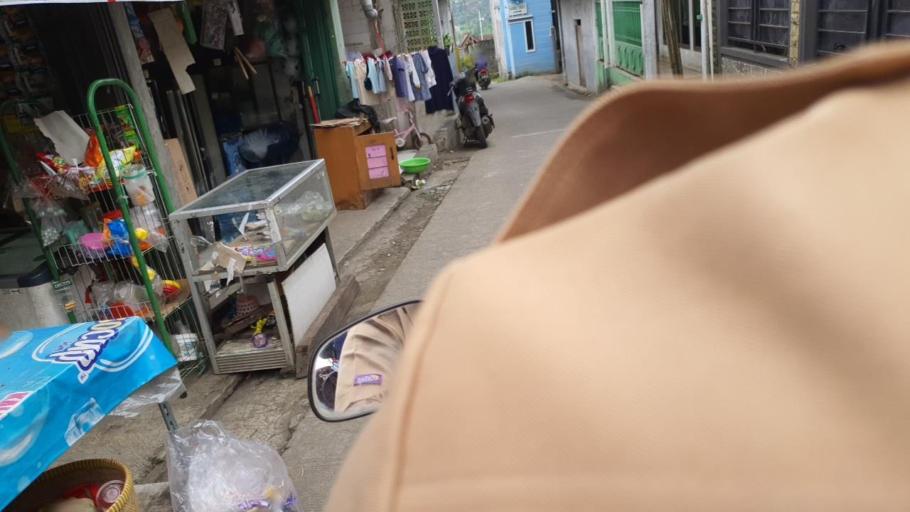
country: ID
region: West Java
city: Caringin
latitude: -6.6508
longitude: 106.8868
